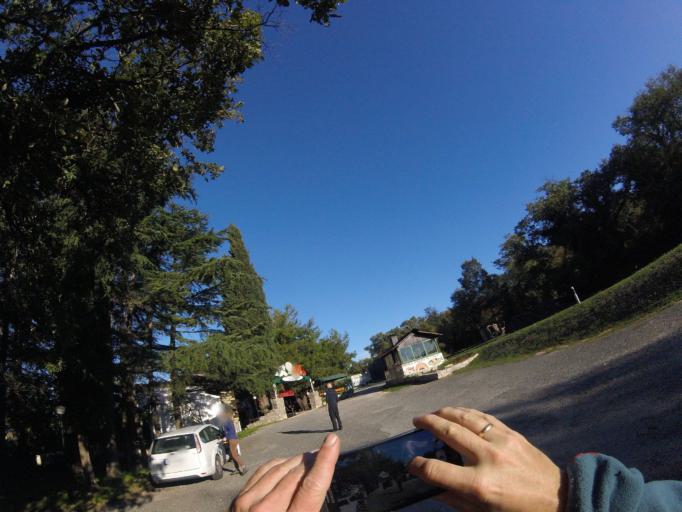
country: HR
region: Istarska
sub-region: Grad Rovinj
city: Rovinj
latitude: 45.1425
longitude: 13.7036
